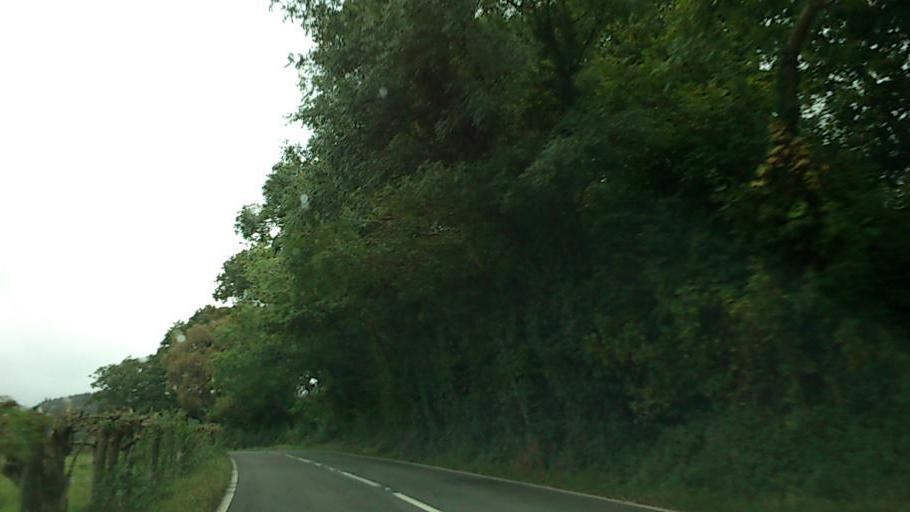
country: GB
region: Wales
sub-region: County of Ceredigion
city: Bow Street
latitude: 52.5284
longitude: -3.9589
